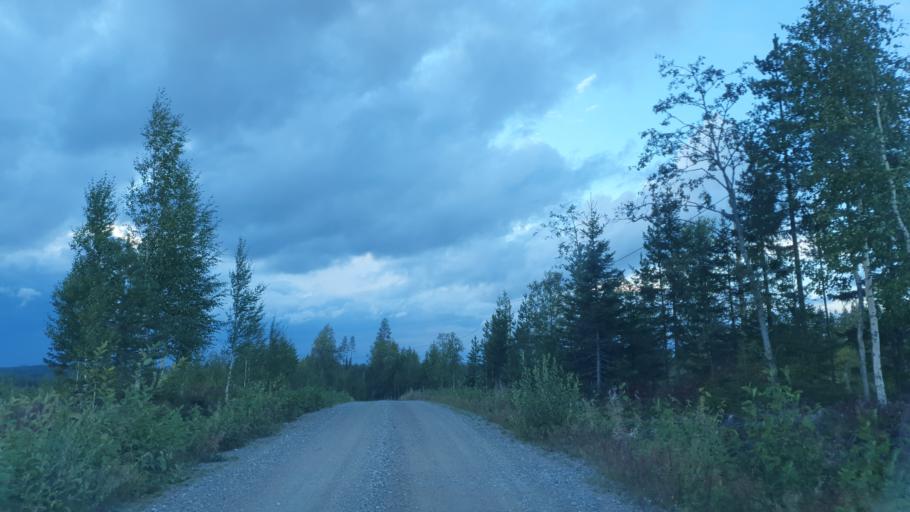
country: FI
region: Kainuu
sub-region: Kehys-Kainuu
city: Kuhmo
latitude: 64.3414
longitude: 29.8811
